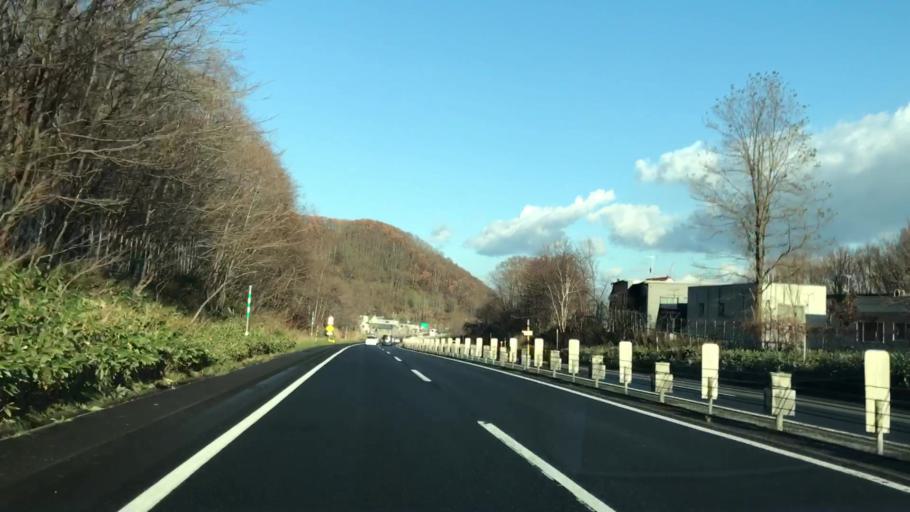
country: JP
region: Hokkaido
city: Sapporo
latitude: 43.1021
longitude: 141.2459
